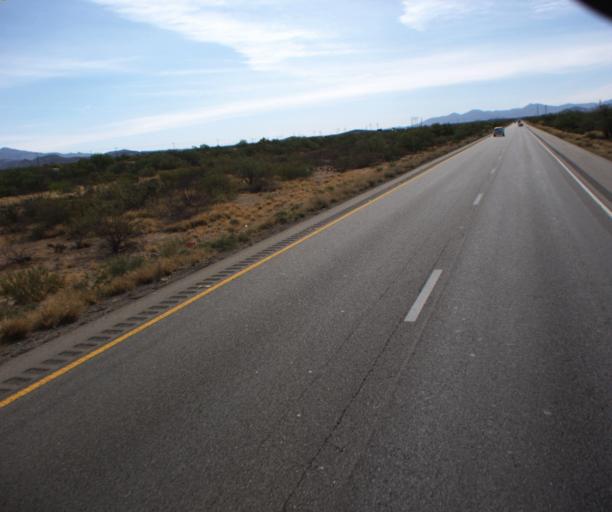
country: US
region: Arizona
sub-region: Pima County
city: Vail
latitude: 32.0442
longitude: -110.7464
